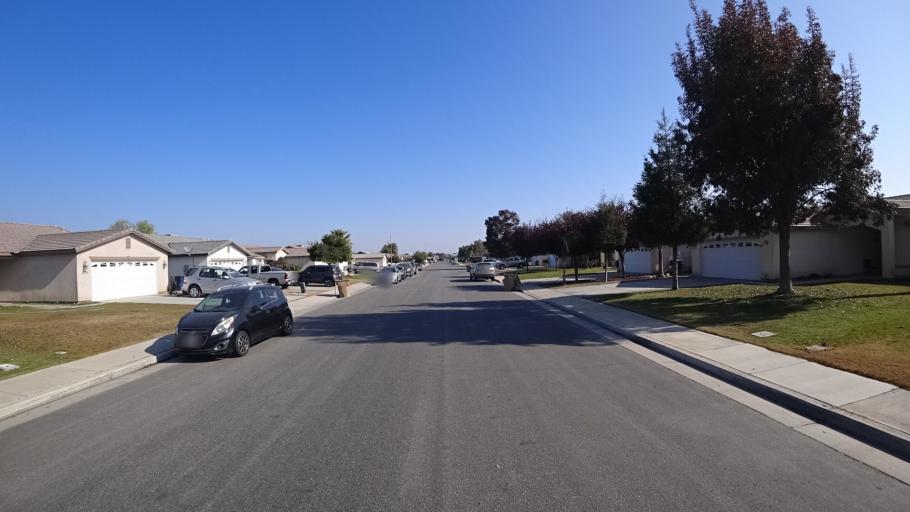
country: US
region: California
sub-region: Kern County
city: Greenfield
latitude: 35.2784
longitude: -119.0183
